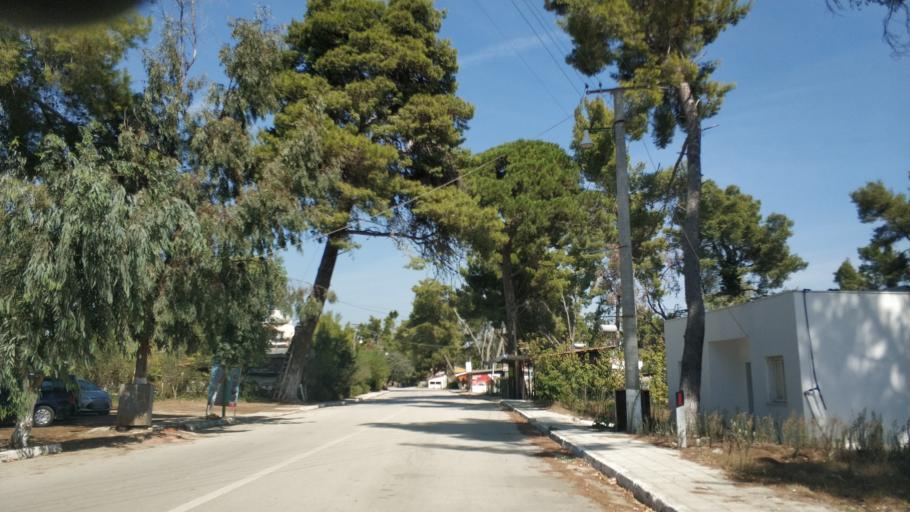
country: AL
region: Fier
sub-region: Rrethi i Lushnjes
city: Divjake
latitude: 40.9690
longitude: 19.4790
